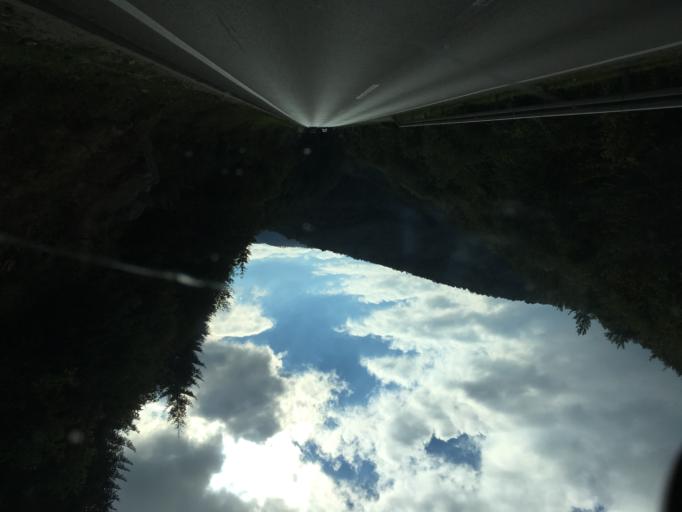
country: BA
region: Federation of Bosnia and Herzegovina
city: Novi Travnik
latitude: 44.0946
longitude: 17.5742
